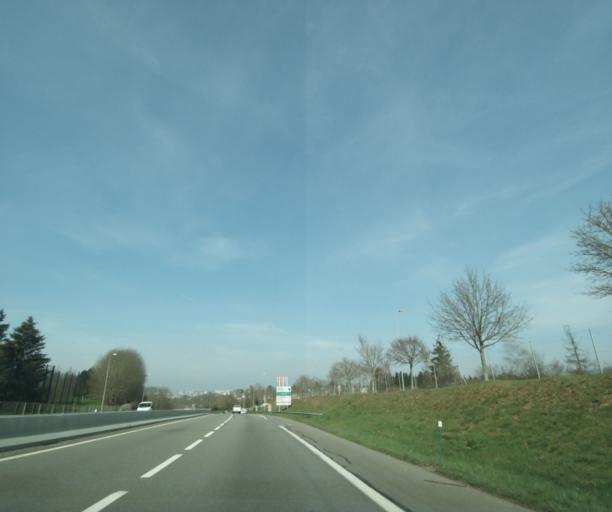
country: FR
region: Limousin
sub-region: Departement de la Haute-Vienne
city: Condat-sur-Vienne
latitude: 45.8155
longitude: 1.2964
